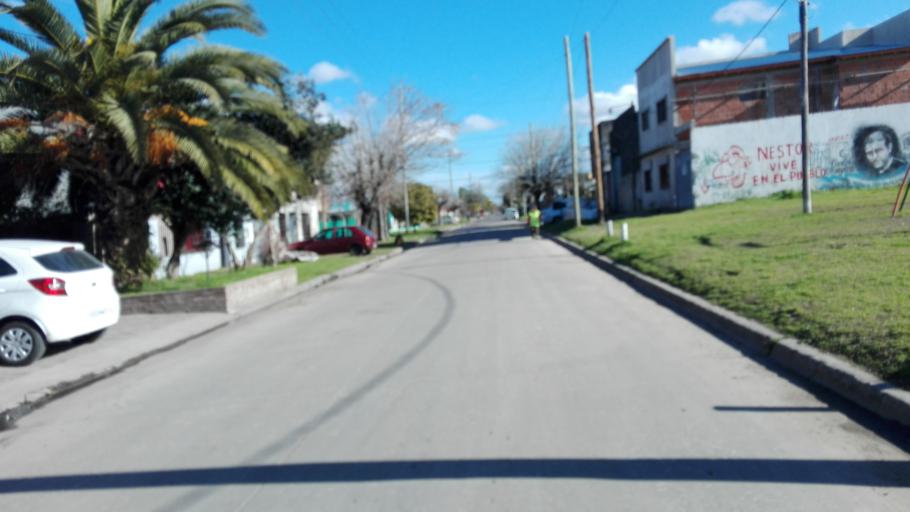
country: AR
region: Buenos Aires
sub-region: Partido de La Plata
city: La Plata
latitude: -34.8827
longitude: -57.9825
